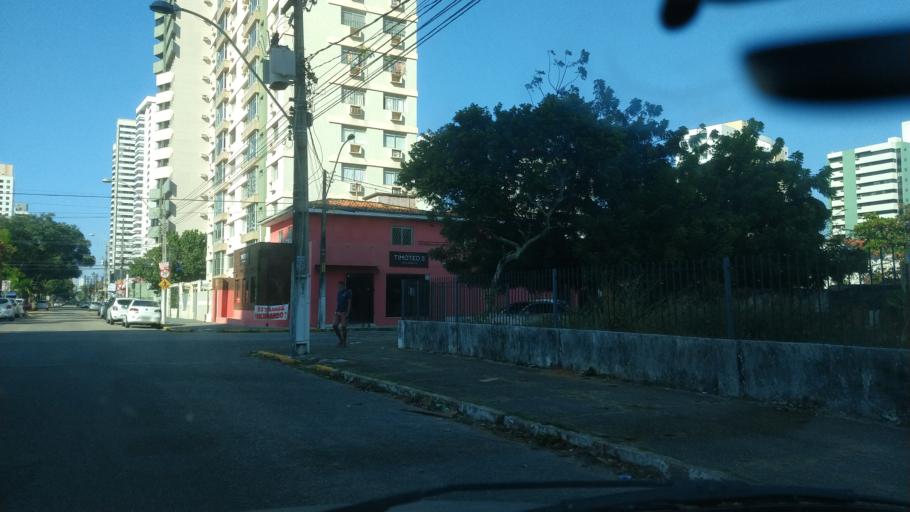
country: BR
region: Rio Grande do Norte
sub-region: Natal
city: Natal
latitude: -5.7859
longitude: -35.1992
